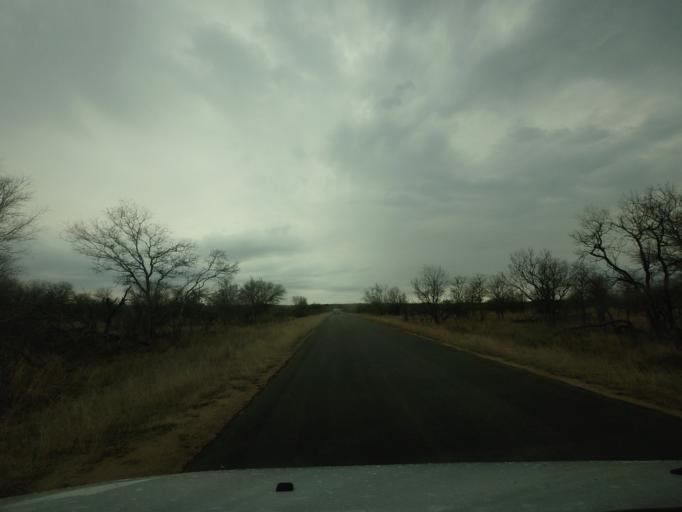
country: ZA
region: Limpopo
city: Thulamahashi
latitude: -24.4700
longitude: 31.4345
